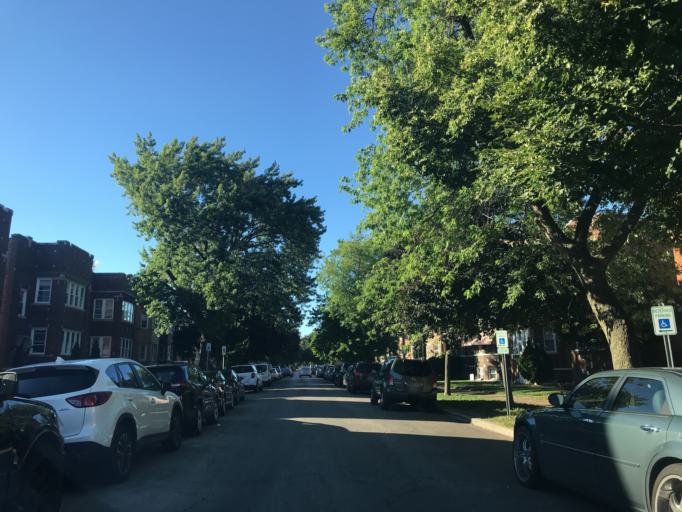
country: US
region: Illinois
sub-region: Cook County
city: Berwyn
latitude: 41.8544
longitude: -87.7862
